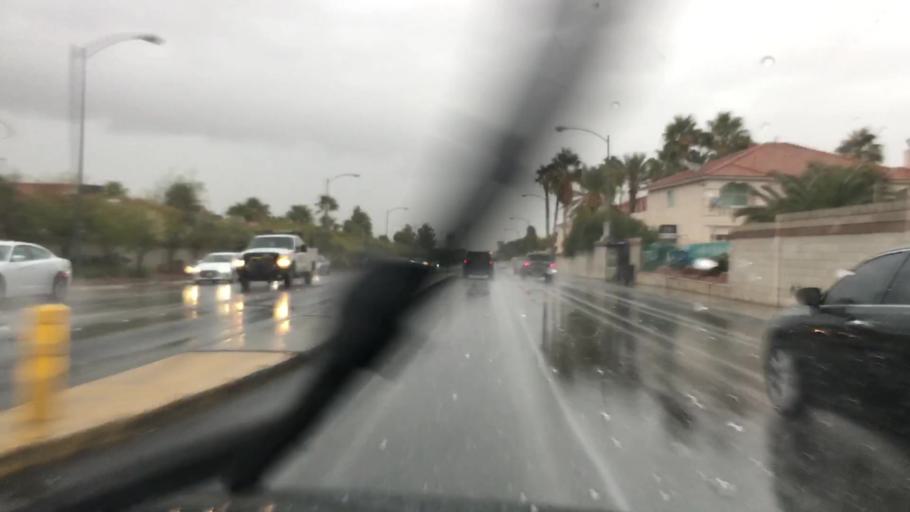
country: US
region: Nevada
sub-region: Clark County
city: Whitney
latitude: 36.0136
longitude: -115.1277
